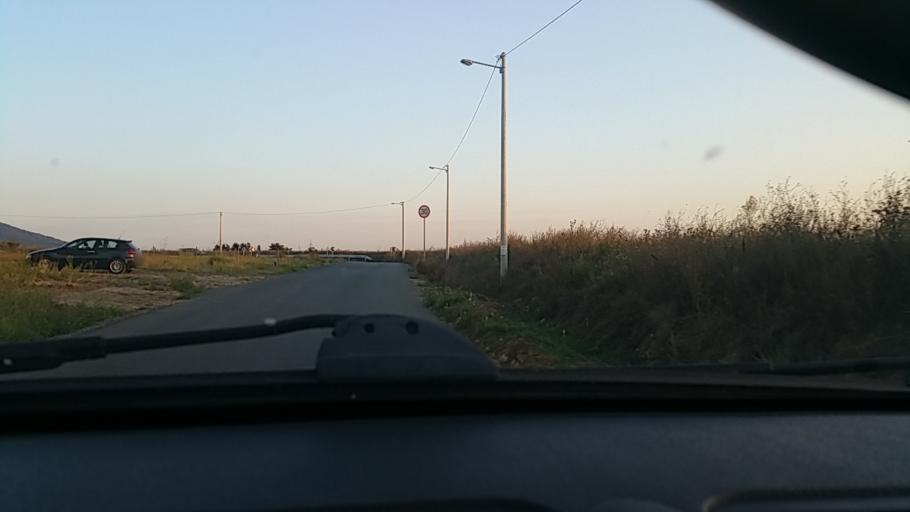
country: RS
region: Central Serbia
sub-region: Belgrade
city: Rakovica
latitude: 44.7275
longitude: 20.4700
